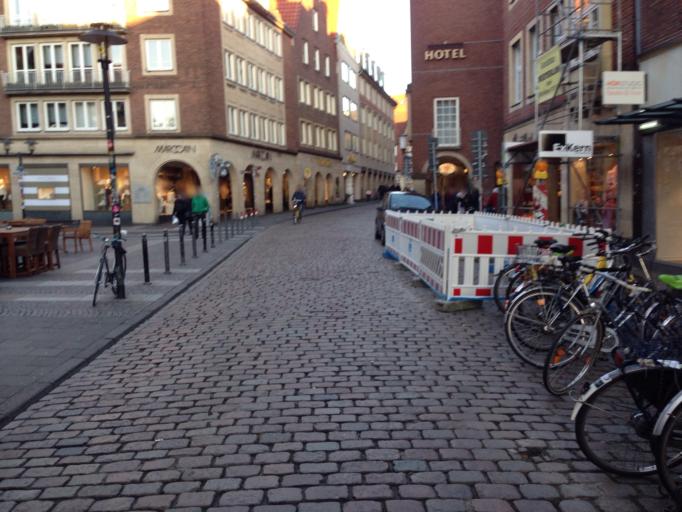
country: DE
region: North Rhine-Westphalia
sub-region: Regierungsbezirk Munster
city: Muenster
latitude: 51.9642
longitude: 7.6259
